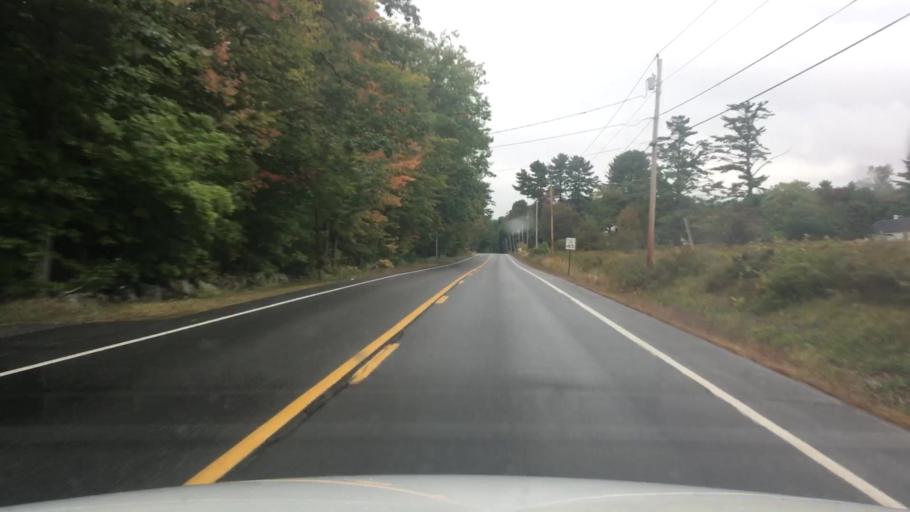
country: US
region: Maine
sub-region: Kennebec County
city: Rome
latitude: 44.5340
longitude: -69.8881
